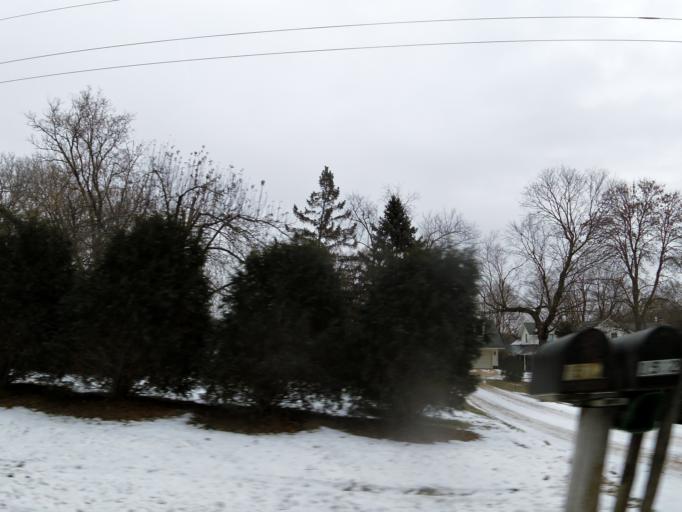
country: US
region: Minnesota
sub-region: Hennepin County
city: Long Lake
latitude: 45.0065
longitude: -93.5839
